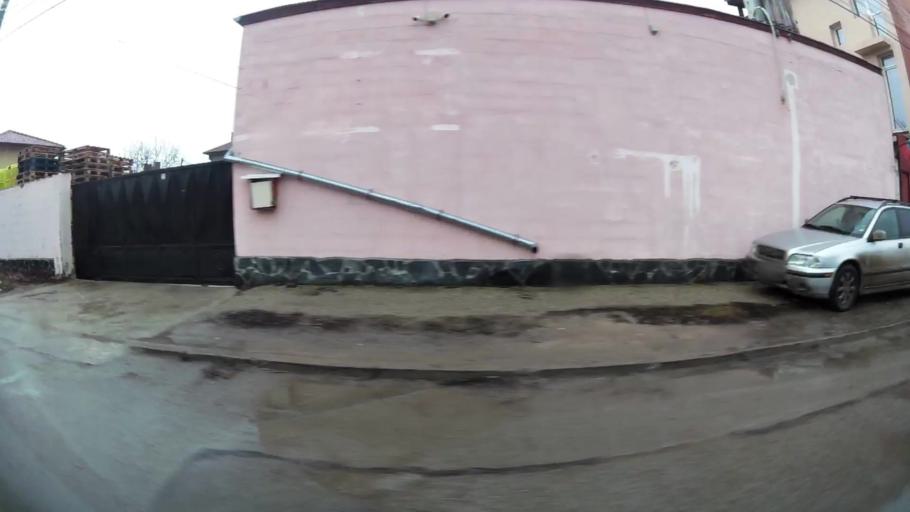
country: BG
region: Sofia-Capital
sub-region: Stolichna Obshtina
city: Sofia
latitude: 42.6329
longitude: 23.4074
